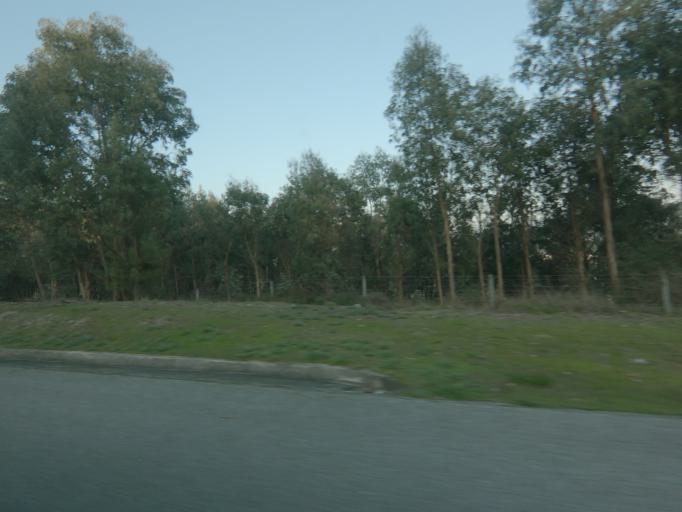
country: PT
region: Porto
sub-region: Marco de Canaveses
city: Marco de Canavezes
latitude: 41.2277
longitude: -8.1745
